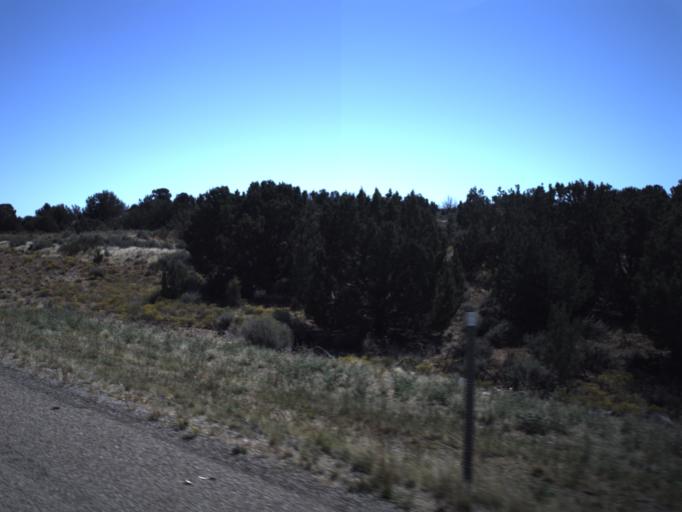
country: US
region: Utah
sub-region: Washington County
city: Ivins
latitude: 37.3198
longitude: -113.6858
